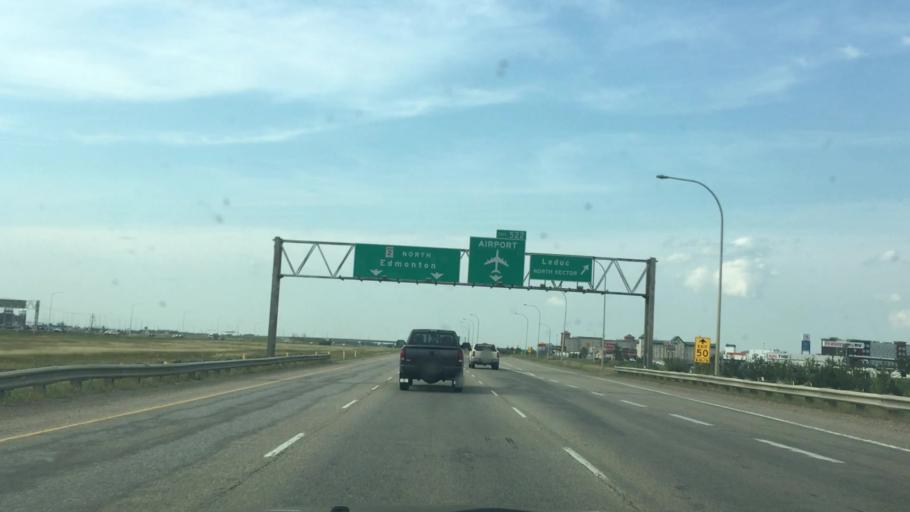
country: CA
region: Alberta
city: Leduc
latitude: 53.2971
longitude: -113.5479
